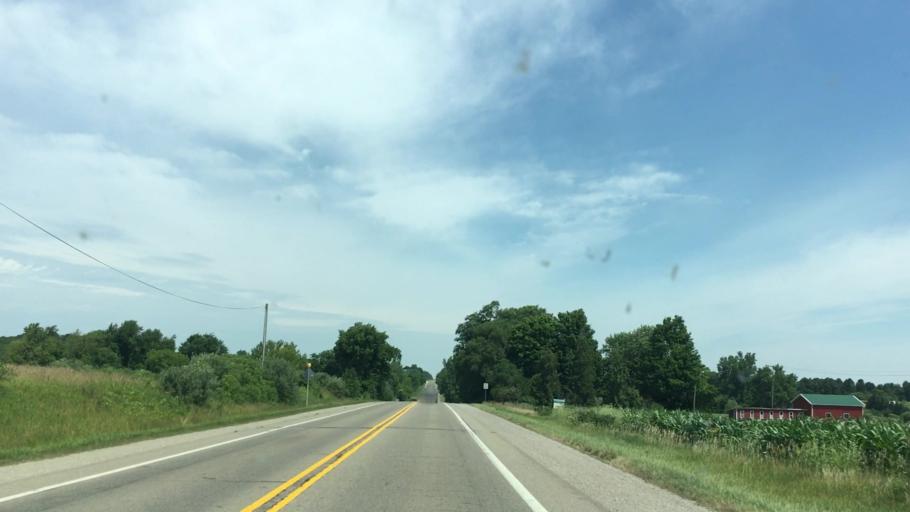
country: US
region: Michigan
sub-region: Lapeer County
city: Imlay City
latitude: 43.1059
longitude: -83.0721
